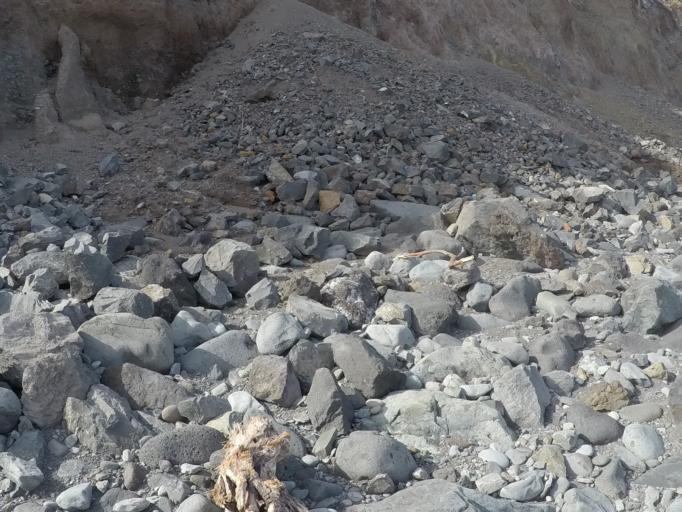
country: PT
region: Madeira
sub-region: Sao Vicente
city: Sao Vicente
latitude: 32.8108
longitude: -16.9709
